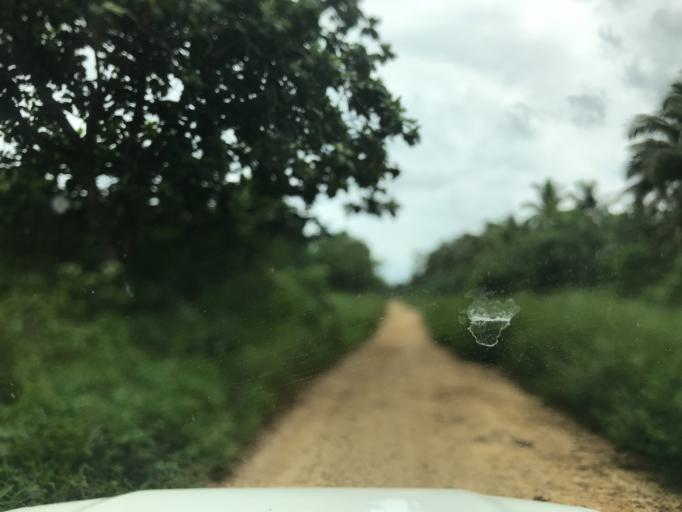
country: VU
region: Sanma
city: Port-Olry
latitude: -15.1856
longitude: 167.0260
